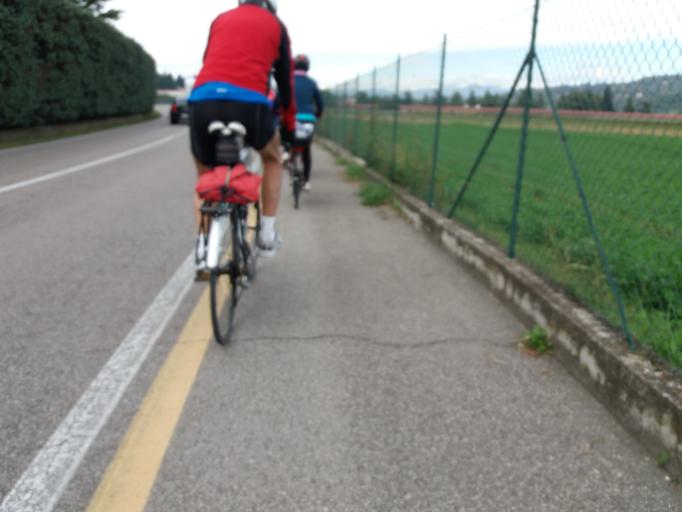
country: IT
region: Veneto
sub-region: Provincia di Verona
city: Calmasino
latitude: 45.5269
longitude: 10.7566
